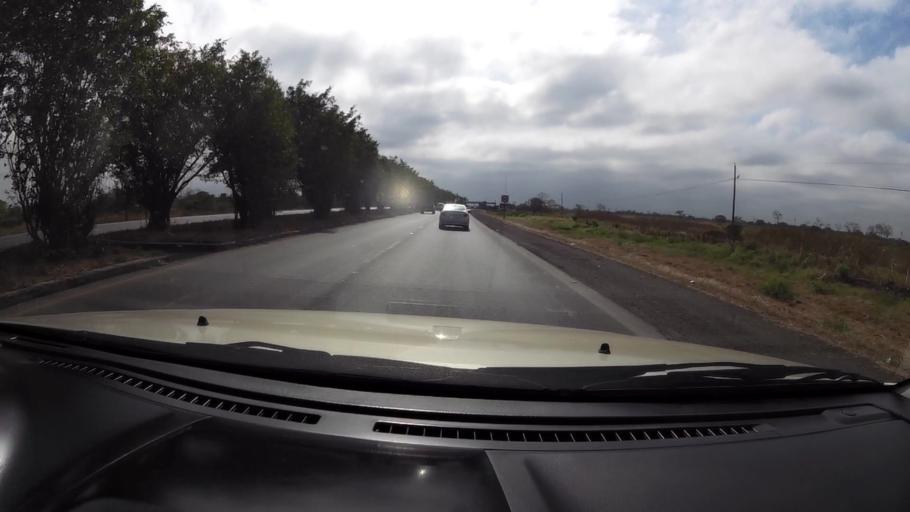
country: EC
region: Guayas
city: Eloy Alfaro
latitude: -2.2008
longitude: -79.7571
